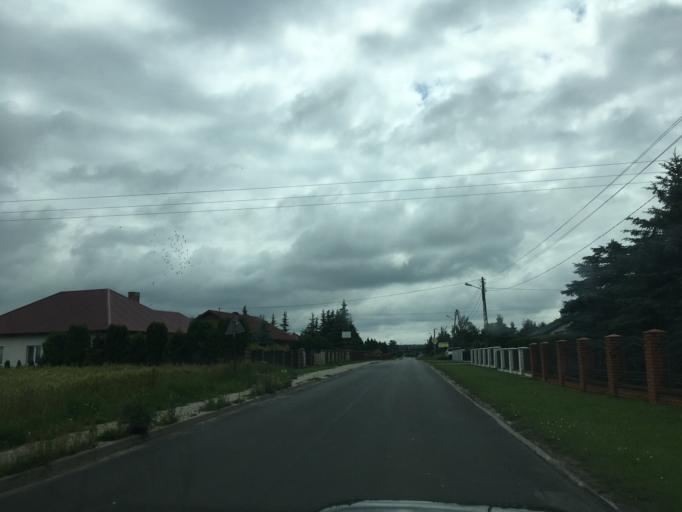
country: PL
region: Lublin Voivodeship
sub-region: Powiat swidnicki
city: Swidnik
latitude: 51.2032
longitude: 22.7336
